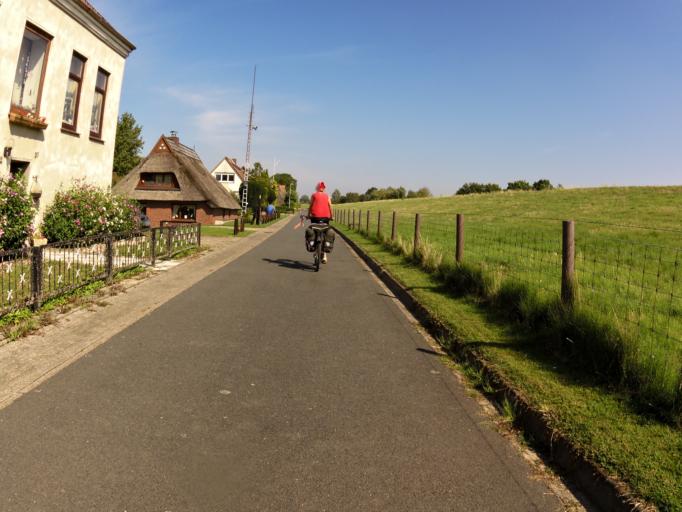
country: DE
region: Lower Saxony
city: Elsfleth
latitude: 53.2576
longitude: 8.4756
